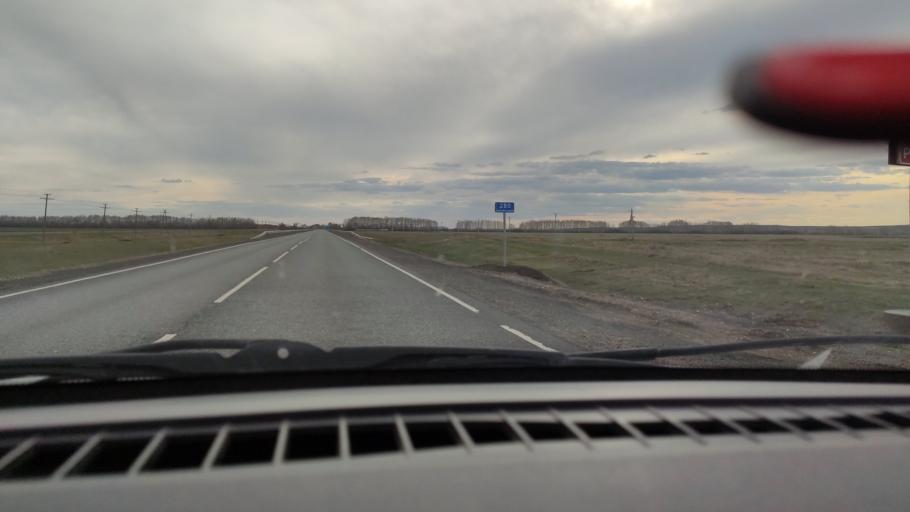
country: RU
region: Bashkortostan
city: Mayachnyy
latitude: 52.3913
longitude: 55.6811
